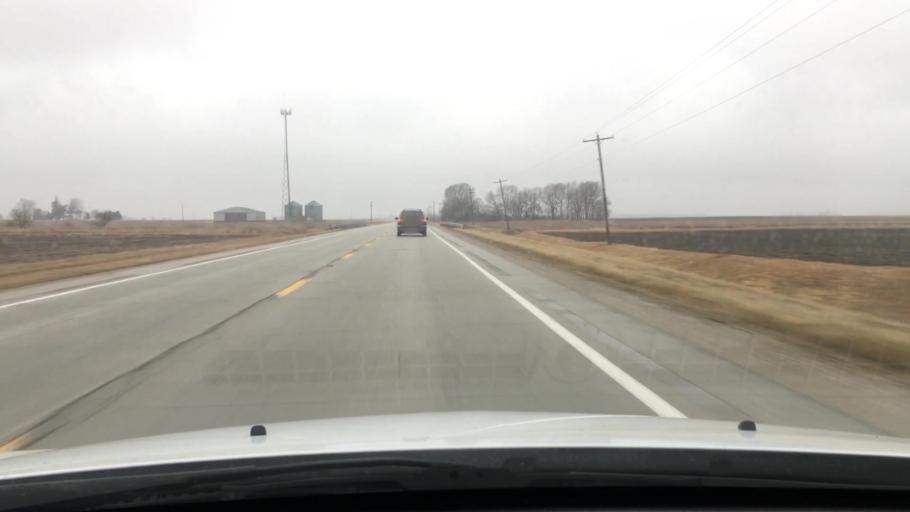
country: US
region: Illinois
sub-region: Livingston County
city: Flanagan
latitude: 40.8719
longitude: -88.8053
